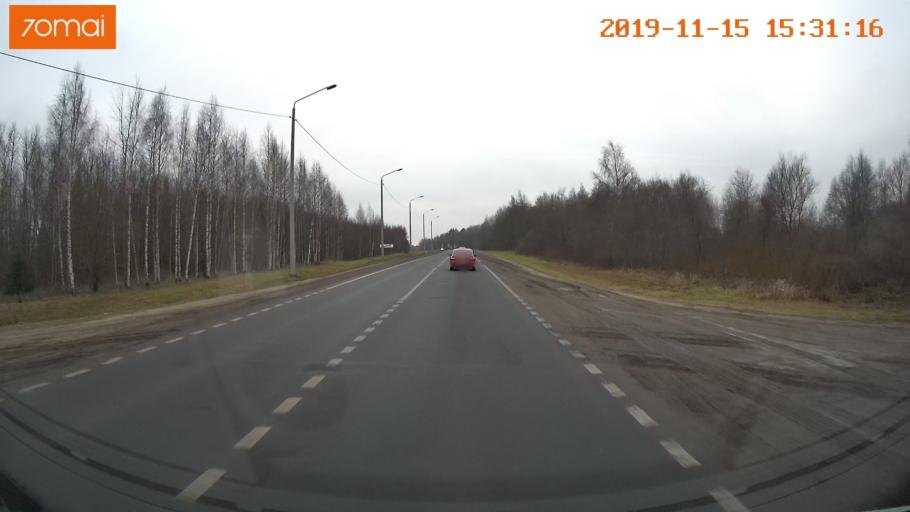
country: RU
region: Jaroslavl
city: Danilov
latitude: 58.1019
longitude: 40.1085
